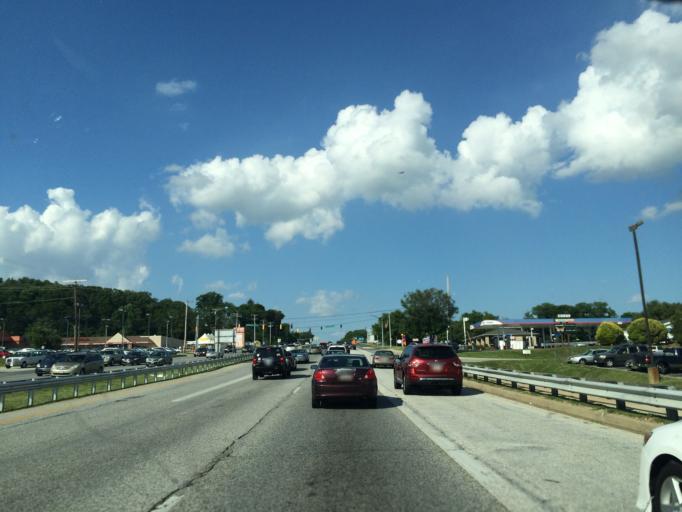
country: US
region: Maryland
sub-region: Howard County
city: Ellicott City
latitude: 39.2840
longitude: -76.8080
